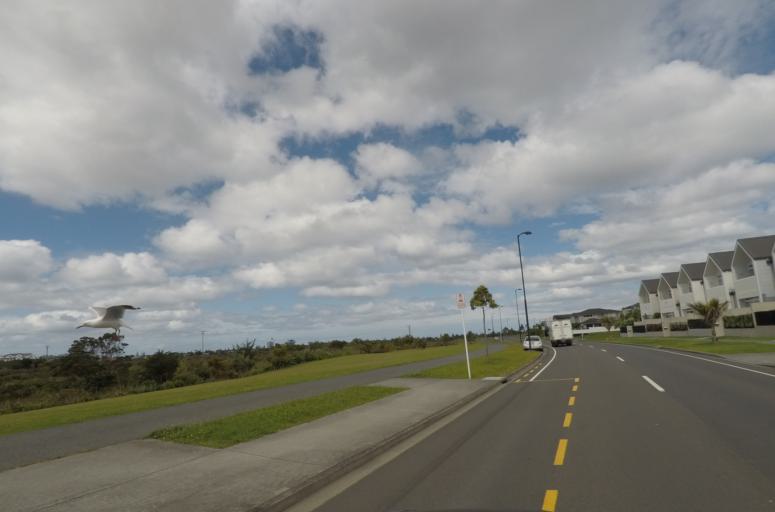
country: NZ
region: Auckland
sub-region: Auckland
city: Rothesay Bay
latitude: -36.5979
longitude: 174.6745
